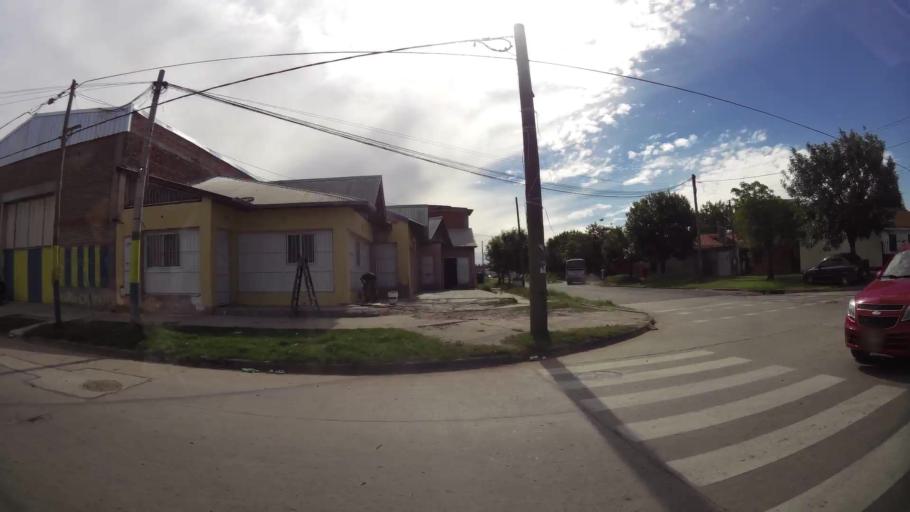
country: AR
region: Santa Fe
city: Granadero Baigorria
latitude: -32.9134
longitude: -60.7139
